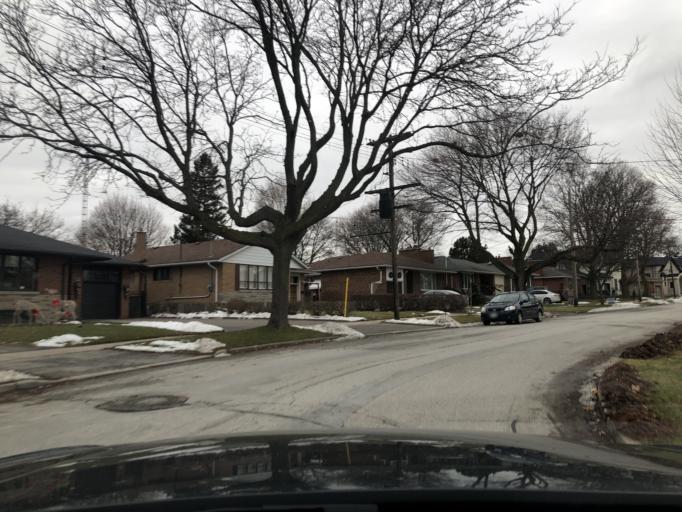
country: CA
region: Ontario
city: Etobicoke
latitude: 43.6906
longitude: -79.5334
